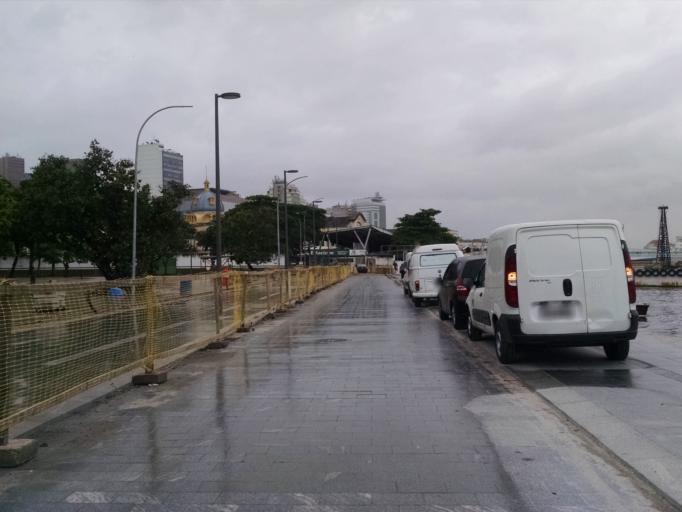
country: BR
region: Rio de Janeiro
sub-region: Rio De Janeiro
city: Rio de Janeiro
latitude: -22.9039
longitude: -43.1704
